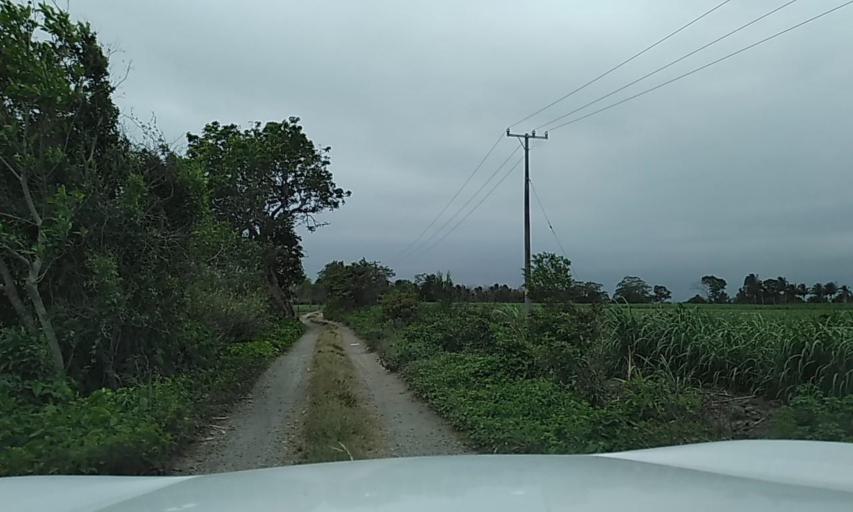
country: MX
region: Veracruz
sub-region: La Antigua
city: Nicolas Blanco (San Pancho)
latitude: 19.3031
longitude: -96.3166
